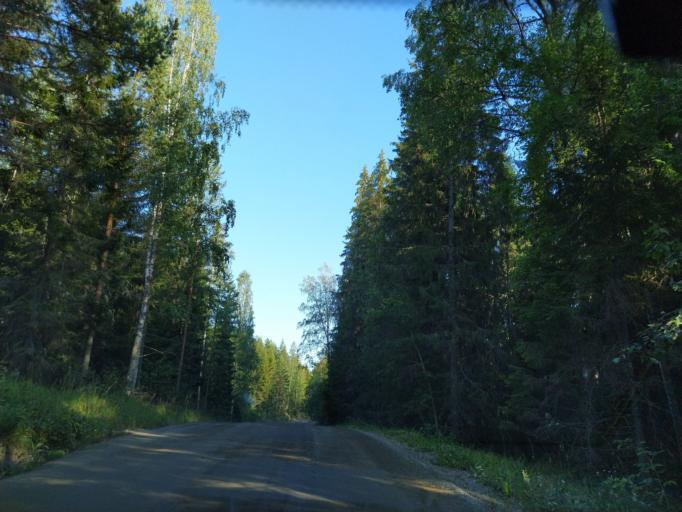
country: FI
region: Central Finland
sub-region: Jaemsae
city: Kuhmoinen
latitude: 61.6263
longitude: 25.0931
